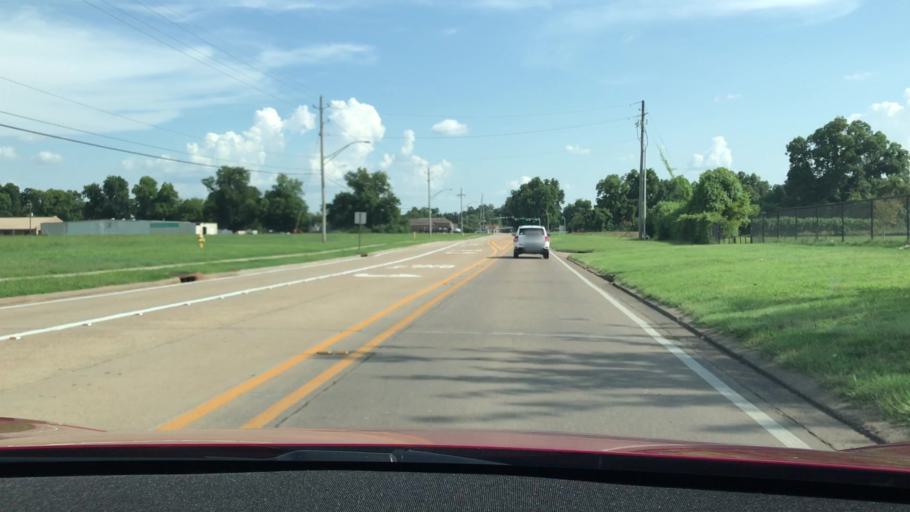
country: US
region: Louisiana
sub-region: Bossier Parish
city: Bossier City
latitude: 32.4622
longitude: -93.6720
